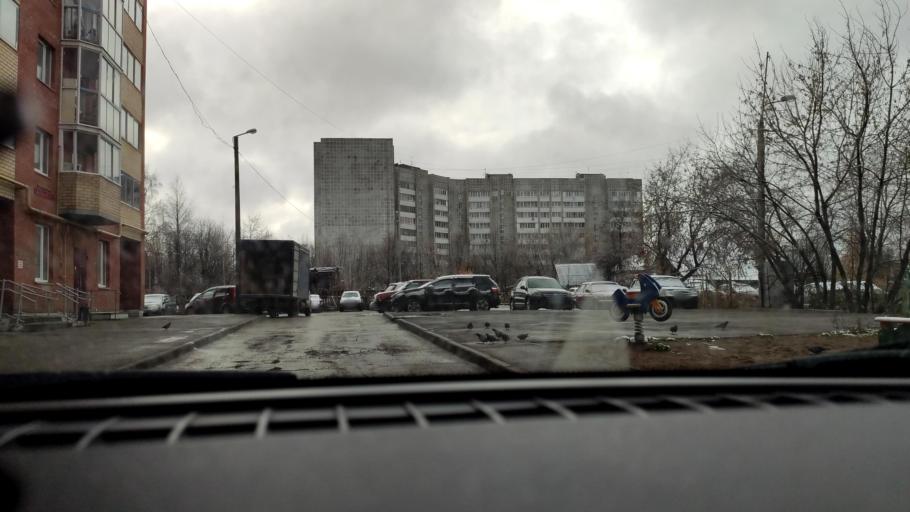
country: RU
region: Perm
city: Perm
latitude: 58.0302
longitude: 56.3263
